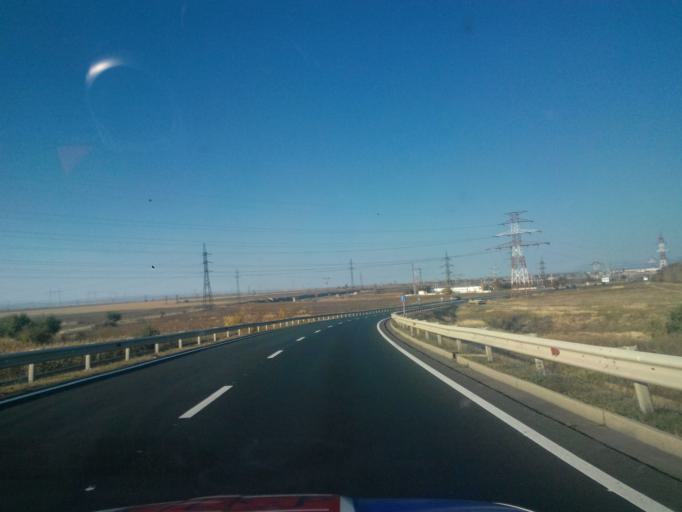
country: RO
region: Vrancea
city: Marasheshty
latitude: 45.8526
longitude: 27.2083
